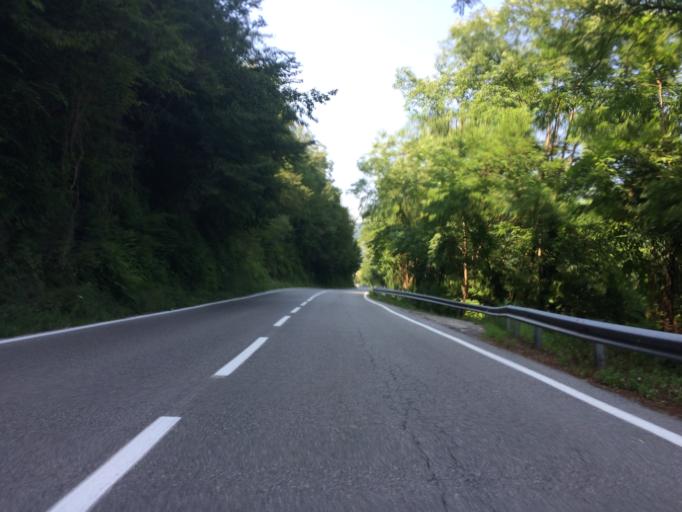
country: IT
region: Piedmont
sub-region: Provincia di Cuneo
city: Torre Bormida
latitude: 44.5665
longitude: 8.1705
